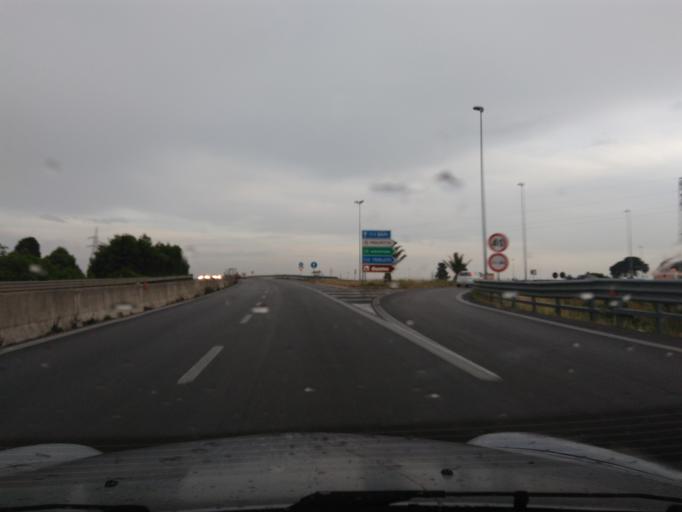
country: IT
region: Apulia
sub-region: Provincia di Bari
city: Molfetta
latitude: 41.1880
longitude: 16.5844
